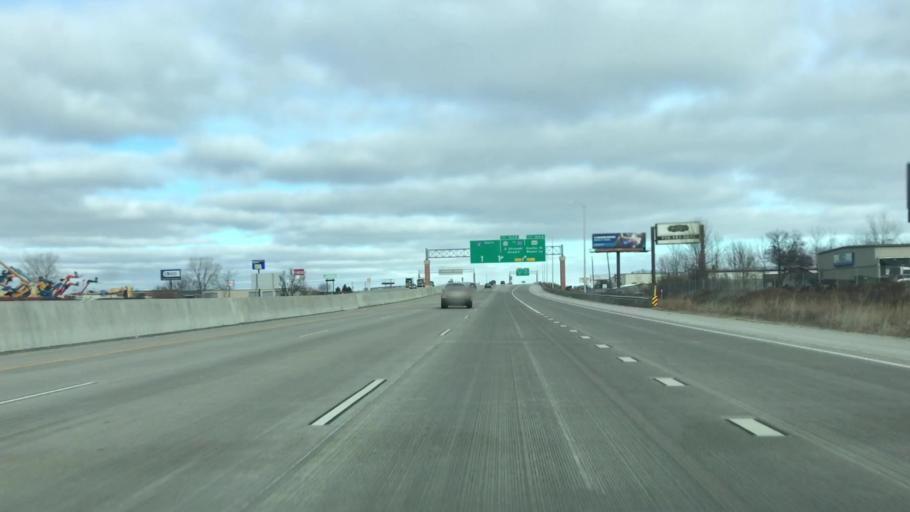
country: US
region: Wisconsin
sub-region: Brown County
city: Ashwaubenon
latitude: 44.4610
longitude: -88.0839
